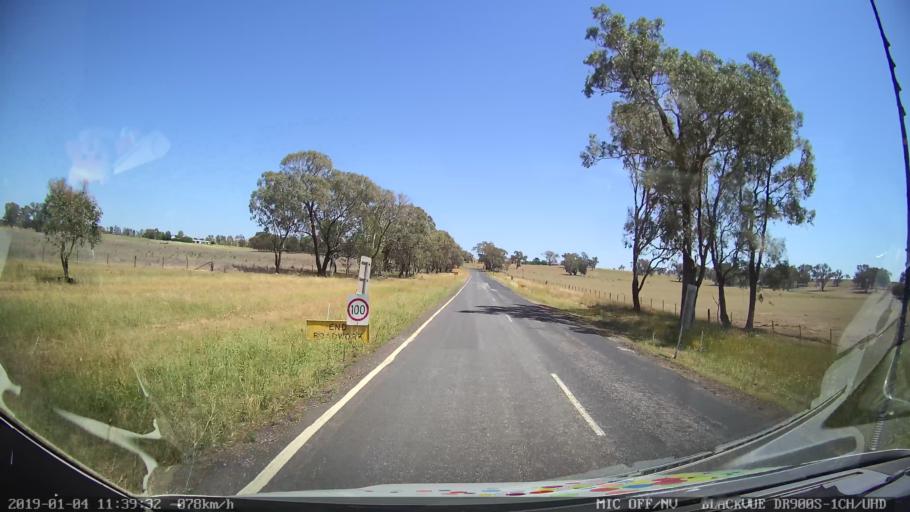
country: AU
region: New South Wales
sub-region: Cabonne
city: Molong
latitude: -33.0124
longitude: 148.7948
